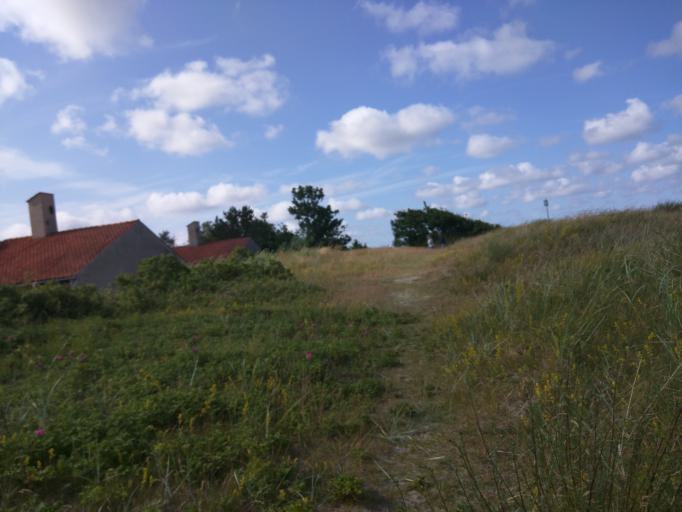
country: DK
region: North Denmark
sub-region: Frederikshavn Kommune
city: Saeby
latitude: 57.3367
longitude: 10.5262
